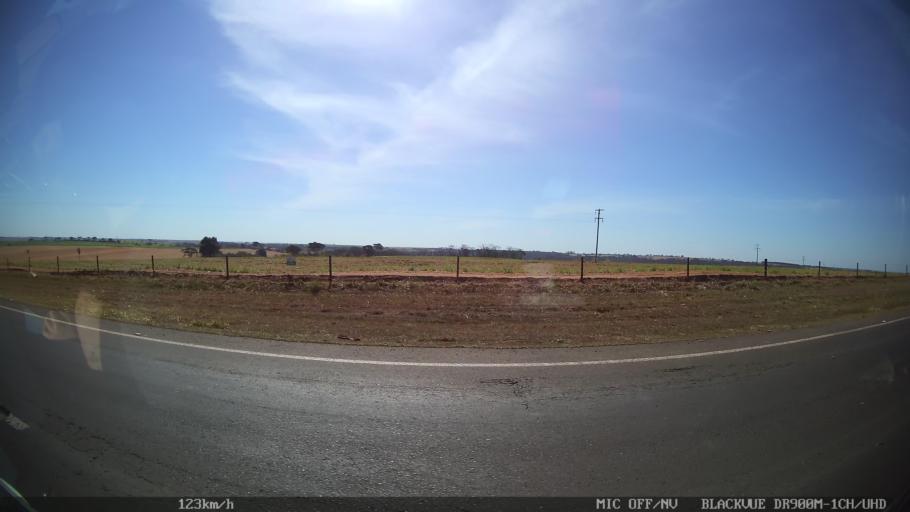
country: BR
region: Sao Paulo
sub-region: Olimpia
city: Olimpia
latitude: -20.6245
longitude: -48.7812
